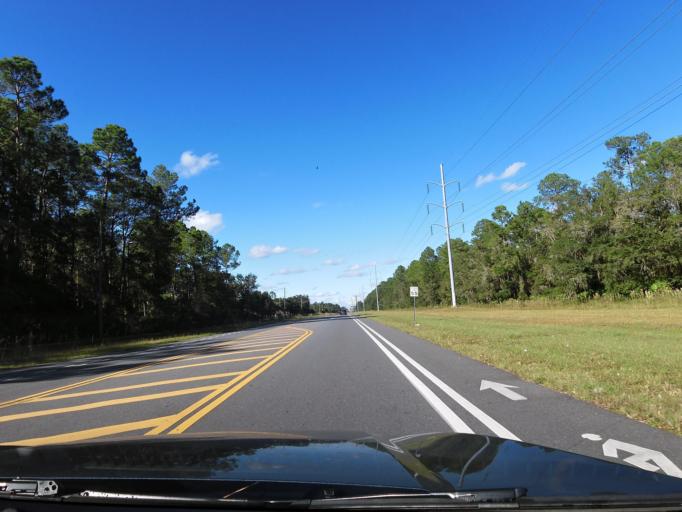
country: US
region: Florida
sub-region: Alachua County
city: Alachua
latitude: 29.7288
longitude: -82.3888
